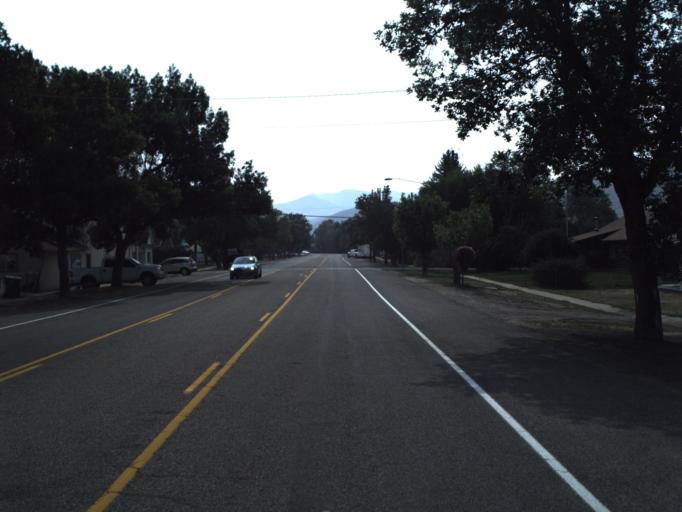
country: US
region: Utah
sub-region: Summit County
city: Coalville
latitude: 41.0177
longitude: -111.4990
